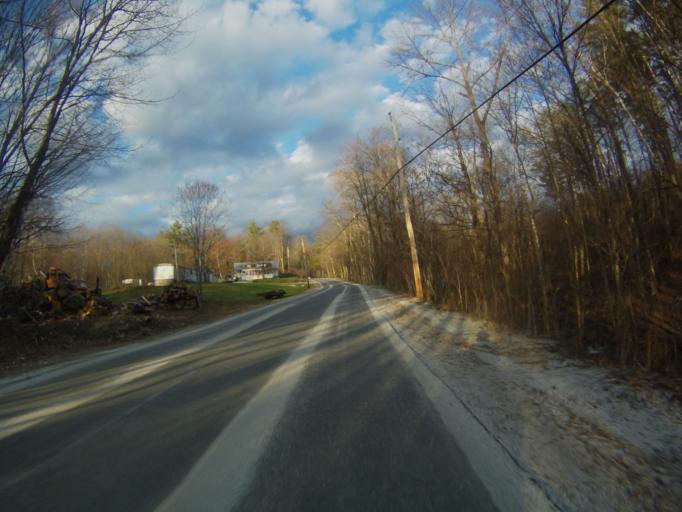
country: US
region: Vermont
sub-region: Rutland County
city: Brandon
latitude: 43.8510
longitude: -73.0195
